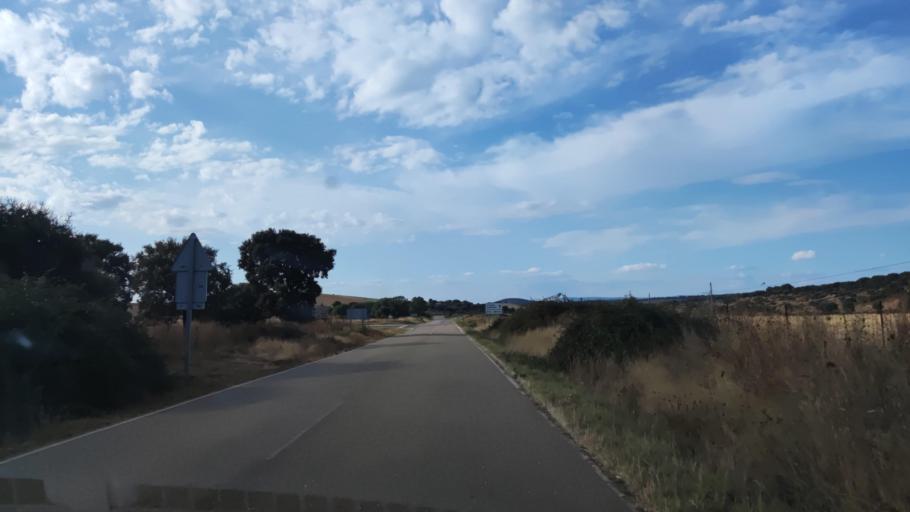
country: ES
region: Castille and Leon
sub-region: Provincia de Salamanca
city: Pastores
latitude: 40.5289
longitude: -6.5233
